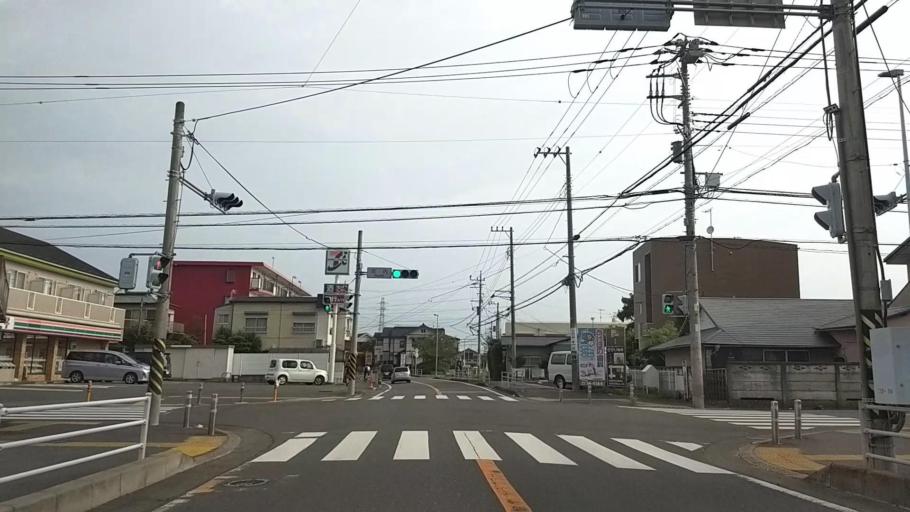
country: JP
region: Kanagawa
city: Oiso
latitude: 35.3370
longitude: 139.3100
